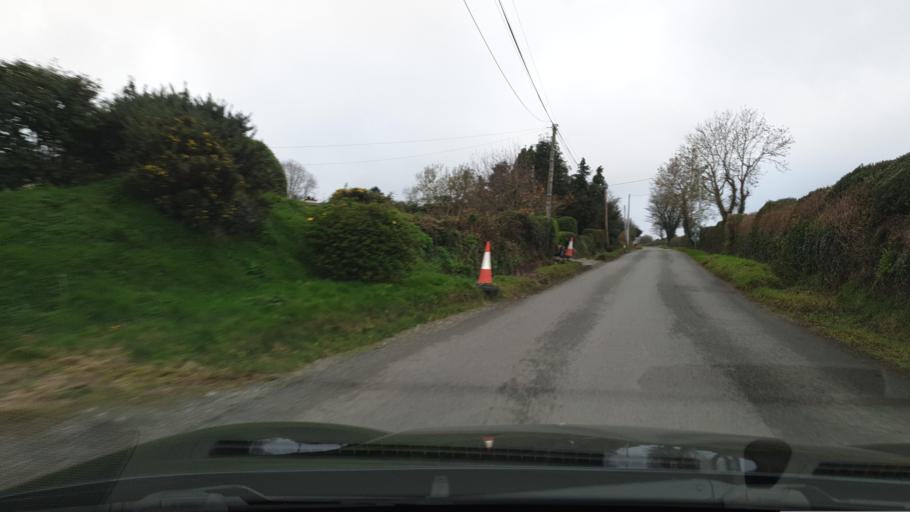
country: IE
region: Leinster
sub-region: Wicklow
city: Enniskerry
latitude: 53.1675
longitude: -6.1782
